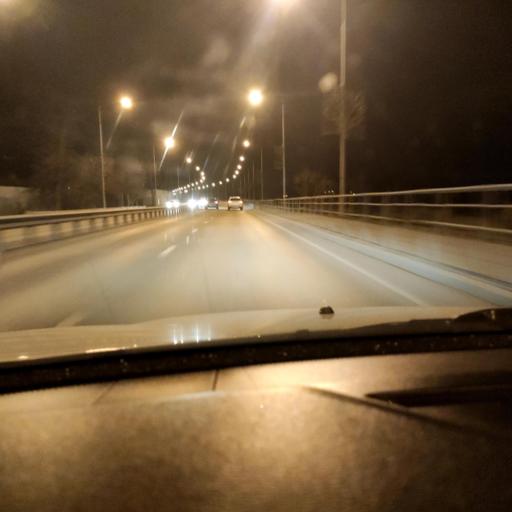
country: RU
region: Samara
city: Volzhskiy
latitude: 53.3996
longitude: 50.1493
